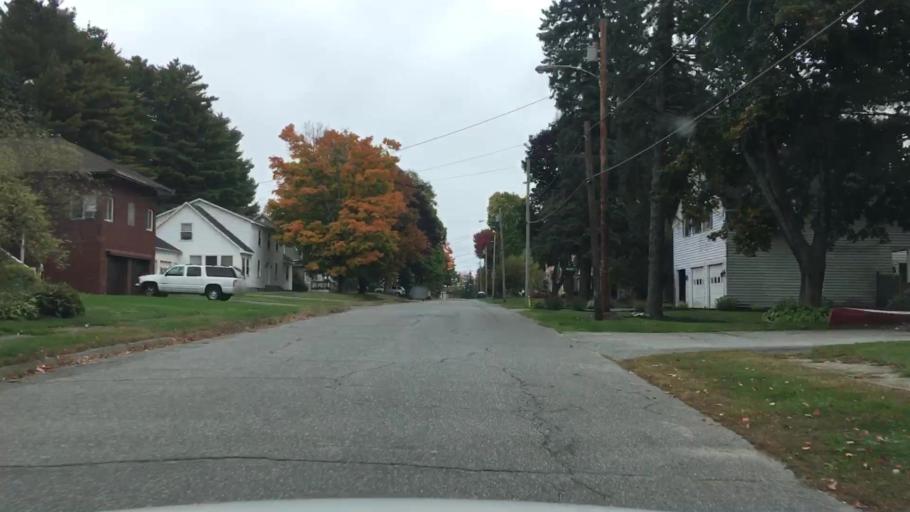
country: US
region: Maine
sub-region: Kennebec County
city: Waterville
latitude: 44.5622
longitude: -69.6398
